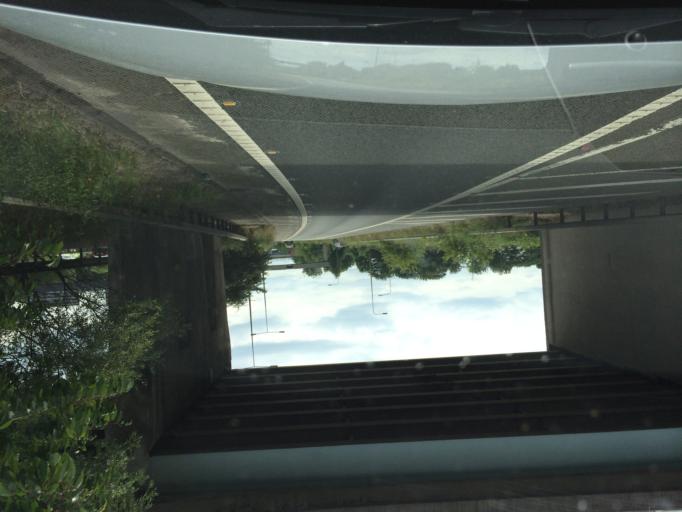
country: GB
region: England
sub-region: Manchester
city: Swinton
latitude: 53.4857
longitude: -2.3758
